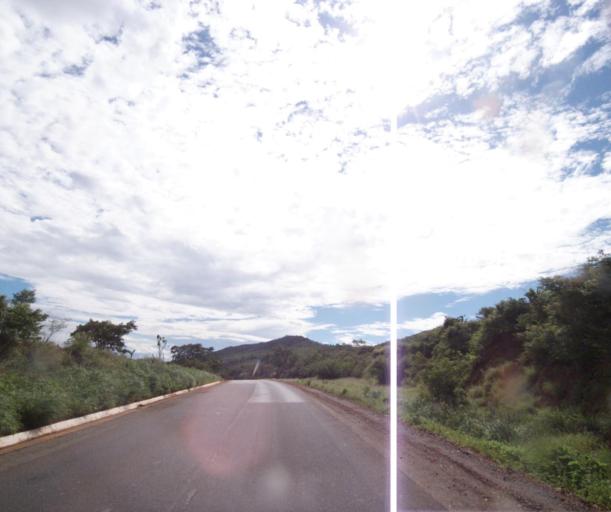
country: BR
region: Minas Gerais
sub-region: Espinosa
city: Espinosa
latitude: -14.7828
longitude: -42.6834
